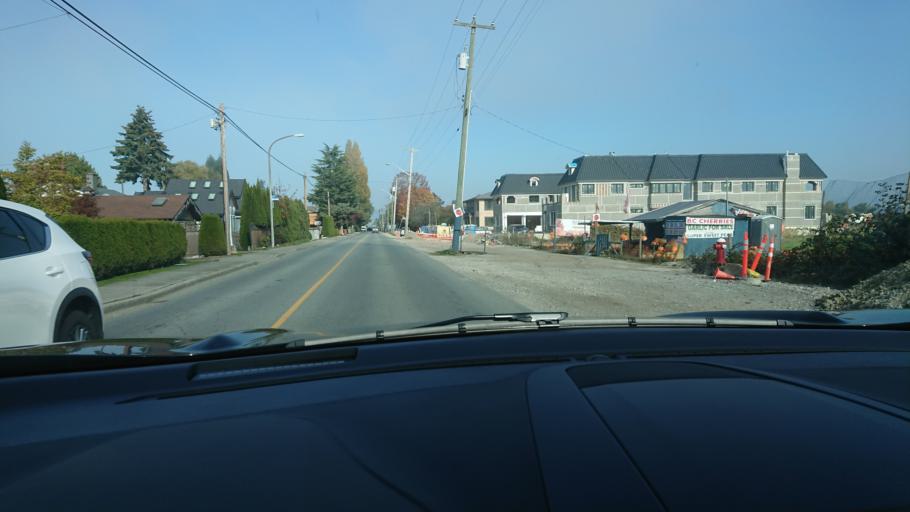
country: CA
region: British Columbia
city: Richmond
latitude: 49.1292
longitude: -123.1589
